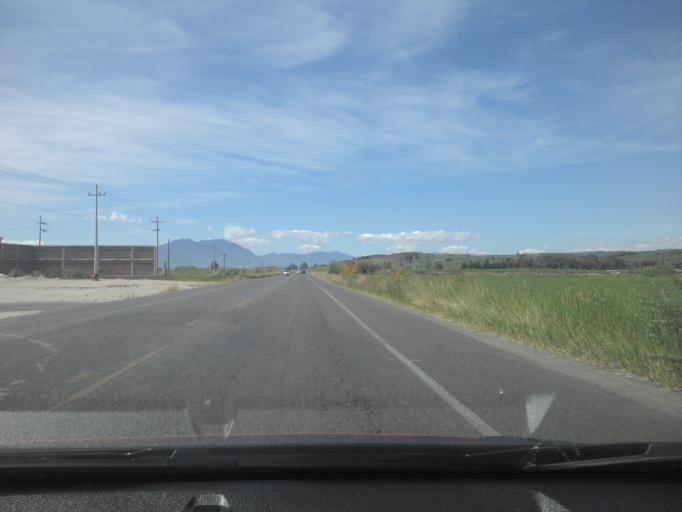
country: MX
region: Jalisco
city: El Refugio
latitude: 20.6664
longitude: -103.7515
